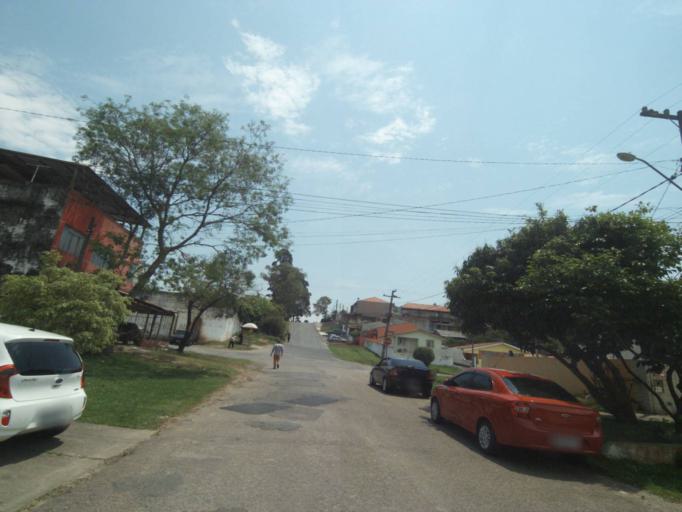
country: BR
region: Parana
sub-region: Pinhais
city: Pinhais
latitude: -25.3992
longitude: -49.2113
